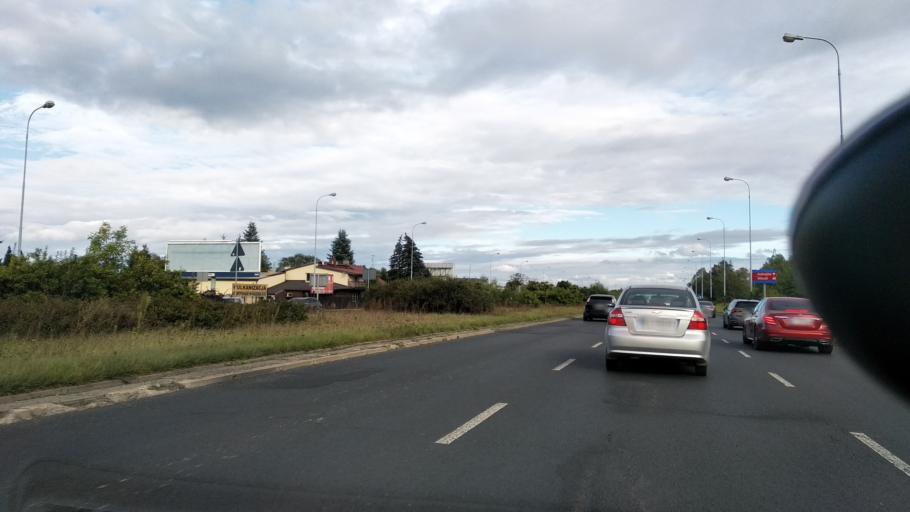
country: PL
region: Lodz Voivodeship
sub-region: Powiat lodzki wschodni
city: Andrespol
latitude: 51.7534
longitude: 19.5770
